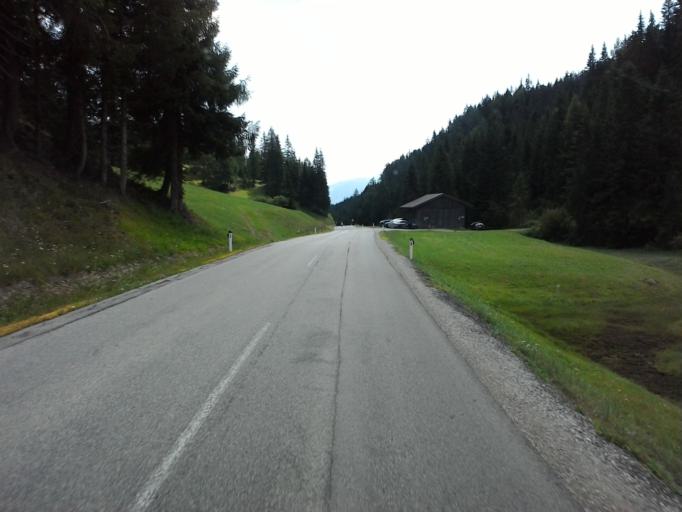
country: AT
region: Tyrol
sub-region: Politischer Bezirk Lienz
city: Abfaltersbach
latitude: 46.7177
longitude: 12.5424
